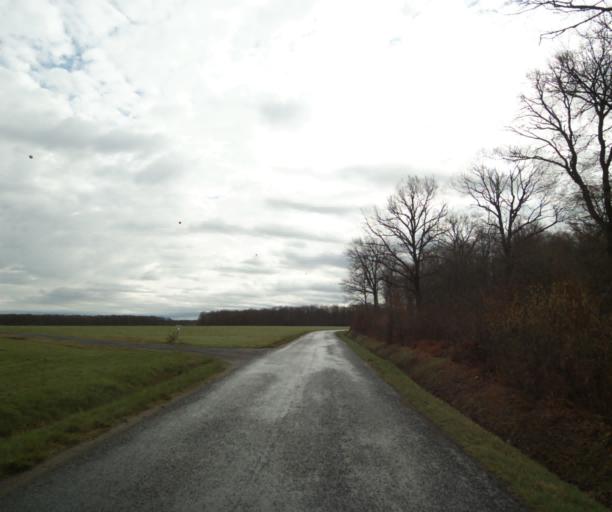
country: FR
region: Auvergne
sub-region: Departement de l'Allier
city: Neuilly-le-Real
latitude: 46.5182
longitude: 3.4326
